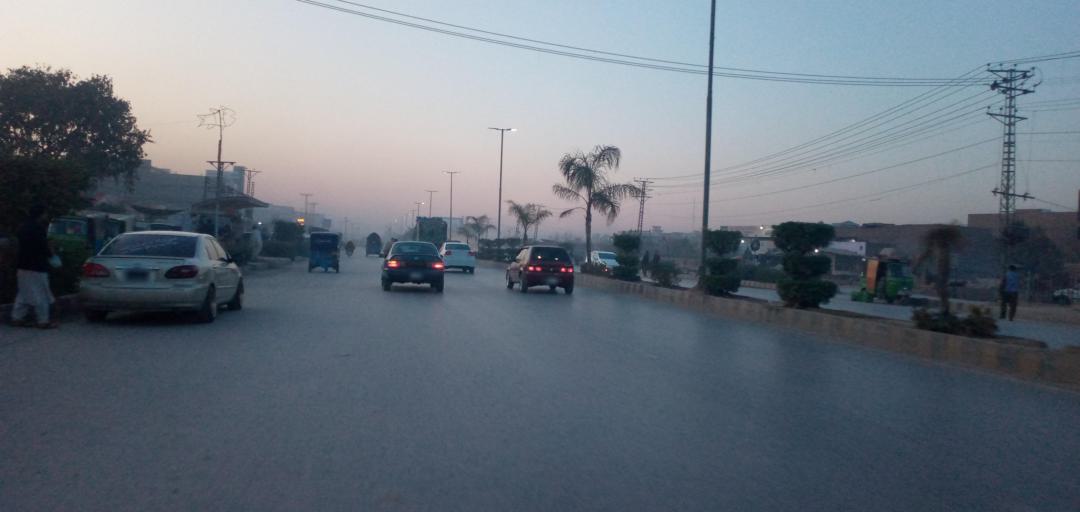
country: PK
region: Khyber Pakhtunkhwa
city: Peshawar
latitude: 34.0302
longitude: 71.6108
